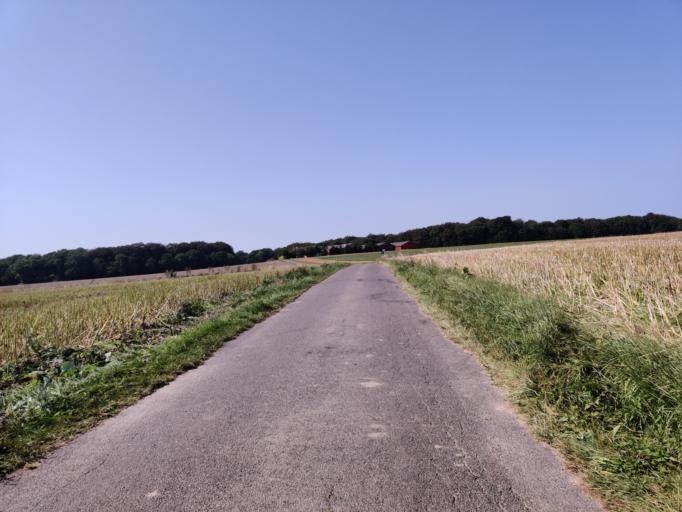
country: DK
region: Zealand
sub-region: Guldborgsund Kommune
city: Nykobing Falster
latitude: 54.6846
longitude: 11.8931
